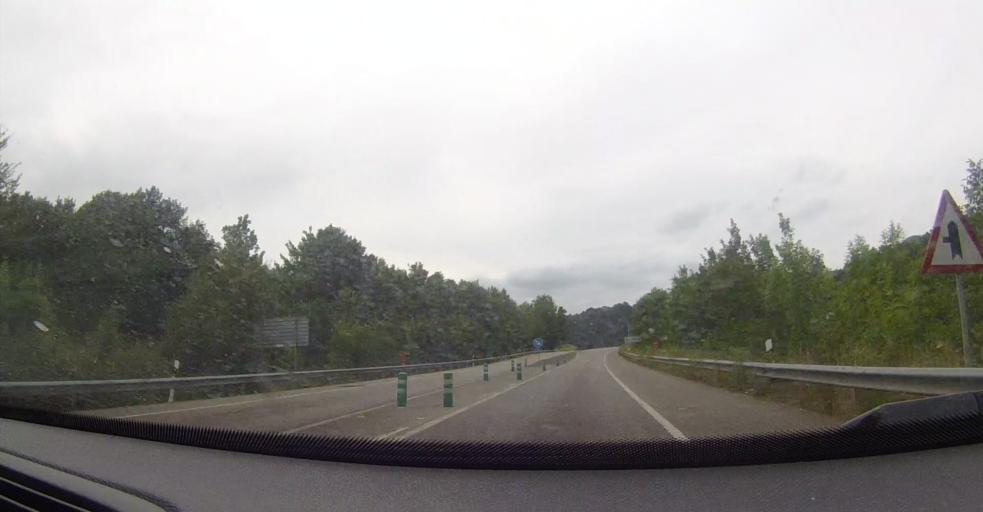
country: ES
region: Asturias
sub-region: Province of Asturias
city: Pilona
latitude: 43.3486
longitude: -5.3404
